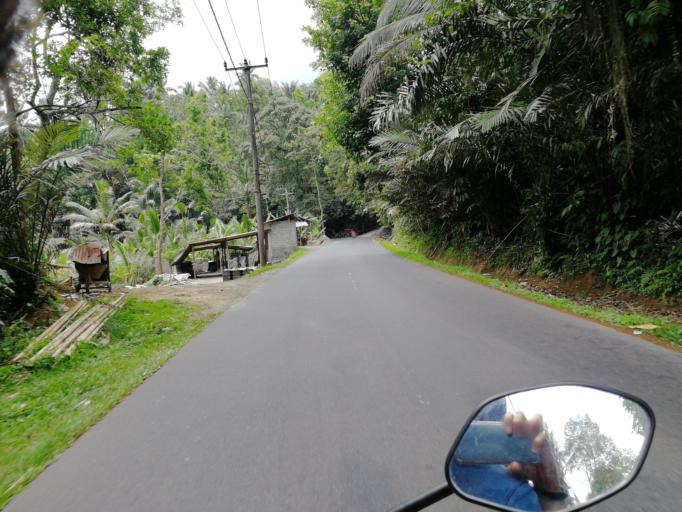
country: ID
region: Bali
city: Banjar Wates Tengah
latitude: -8.4535
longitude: 115.4571
